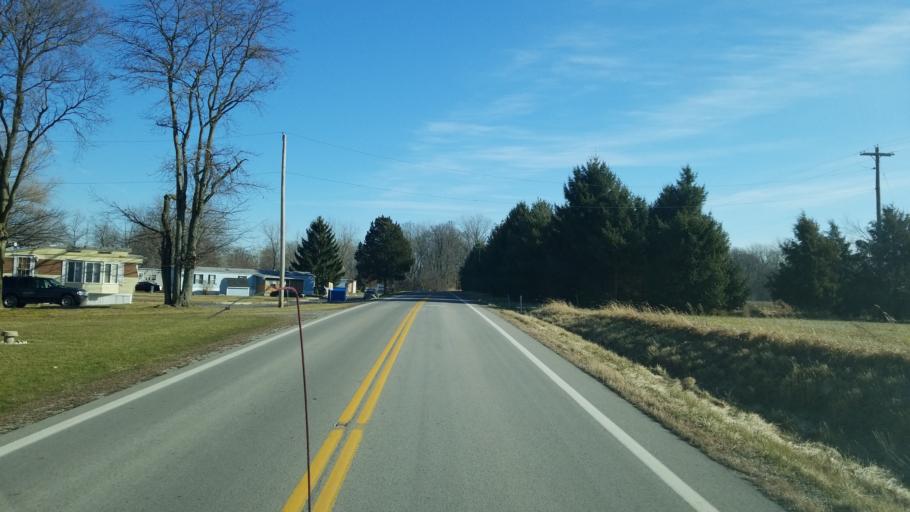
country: US
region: Ohio
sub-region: Henry County
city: Liberty Center
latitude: 41.4149
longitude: -83.9225
